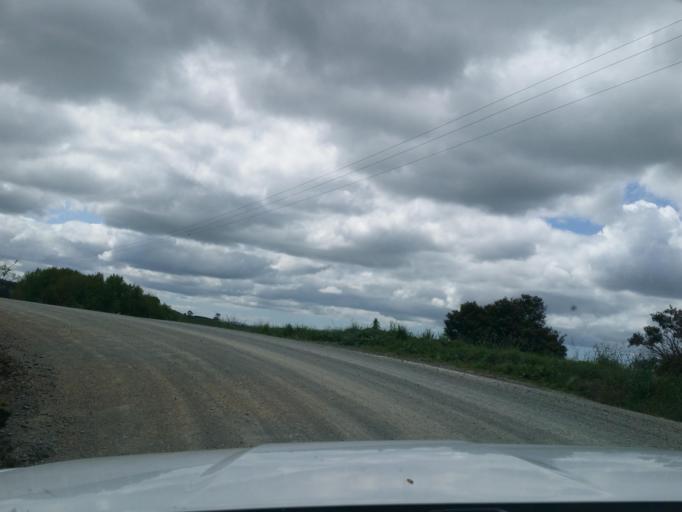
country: NZ
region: Auckland
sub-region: Auckland
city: Wellsford
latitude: -36.2505
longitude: 174.3661
